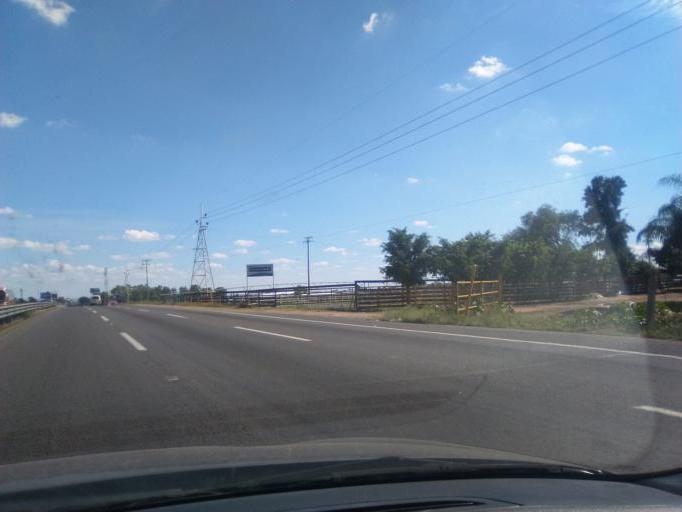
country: MX
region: Guanajuato
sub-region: Silao de la Victoria
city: San Antonio Texas
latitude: 20.9949
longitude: -101.5008
